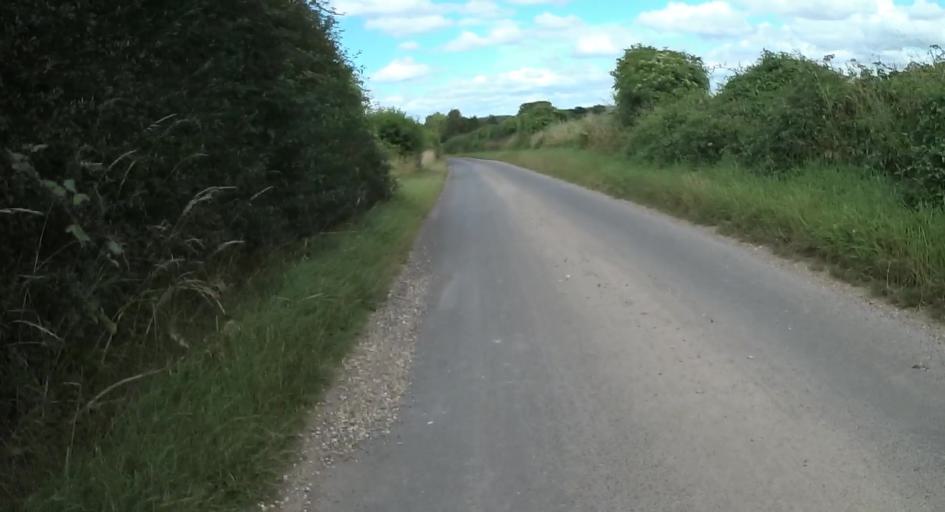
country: GB
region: England
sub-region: Hampshire
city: Kings Worthy
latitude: 51.1607
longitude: -1.3064
